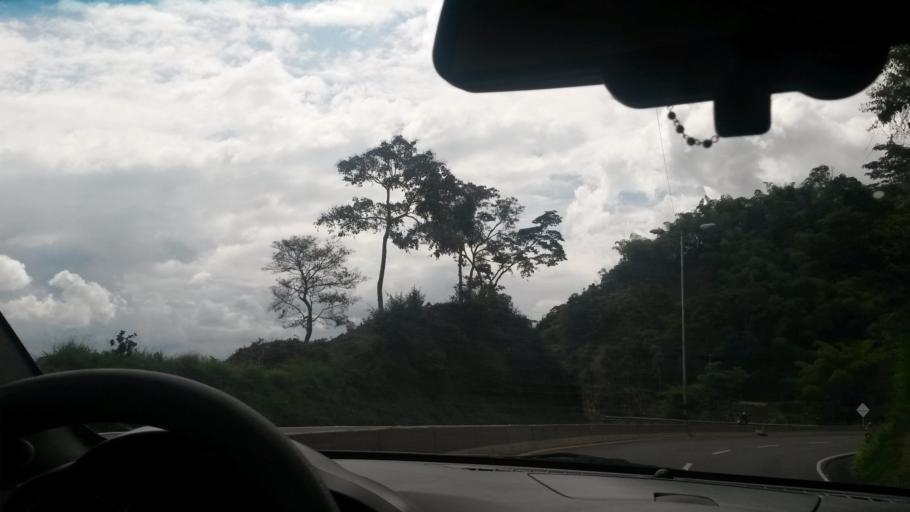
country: CO
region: Caldas
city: Manizales
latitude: 5.0537
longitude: -75.5632
